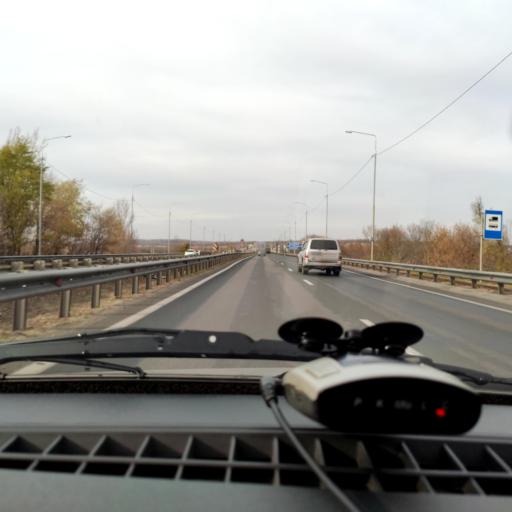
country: RU
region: Voronezj
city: Pridonskoy
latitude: 51.6499
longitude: 39.0811
